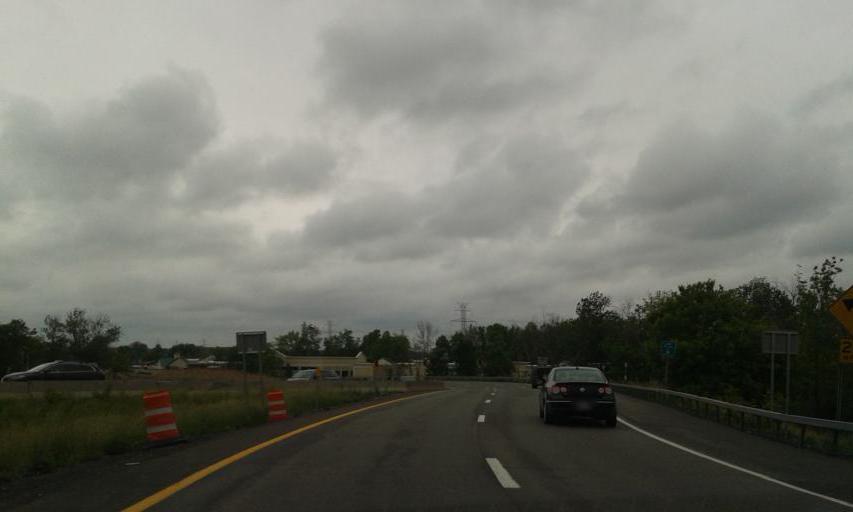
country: US
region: New York
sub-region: Erie County
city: Amherst
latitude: 43.0040
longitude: -78.8193
